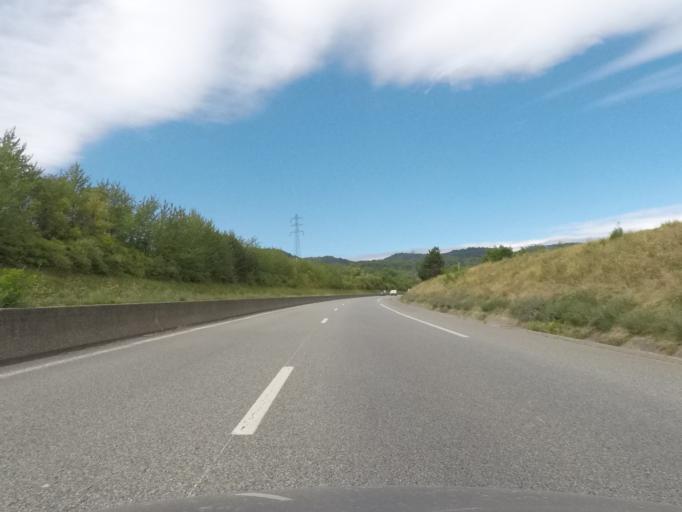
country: FR
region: Auvergne
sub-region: Departement du Puy-de-Dome
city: Beaumont
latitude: 45.7428
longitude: 3.0839
